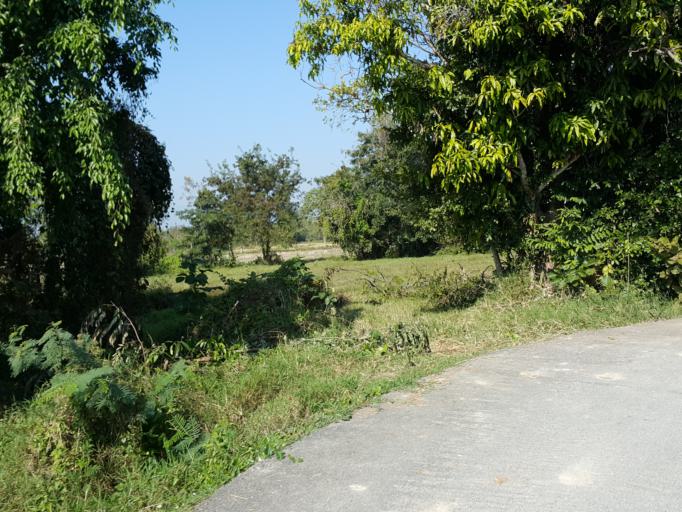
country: TH
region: Chiang Mai
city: San Sai
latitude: 18.8073
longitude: 99.0959
